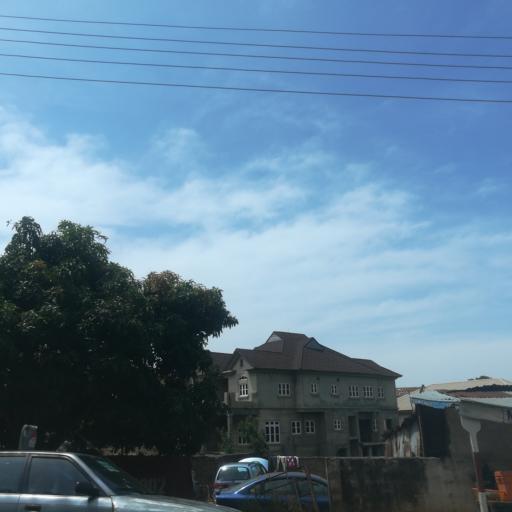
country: NG
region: Plateau
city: Jos
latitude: 9.9037
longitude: 8.8864
